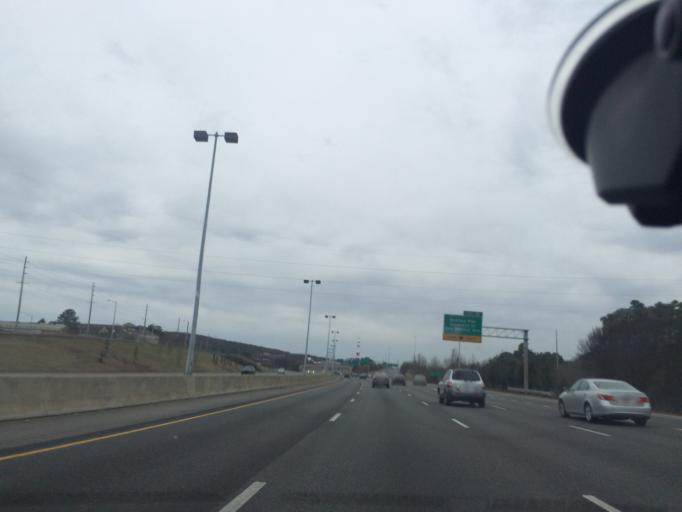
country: US
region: Alabama
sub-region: Madison County
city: Redstone Arsenal
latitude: 34.7180
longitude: -86.6357
